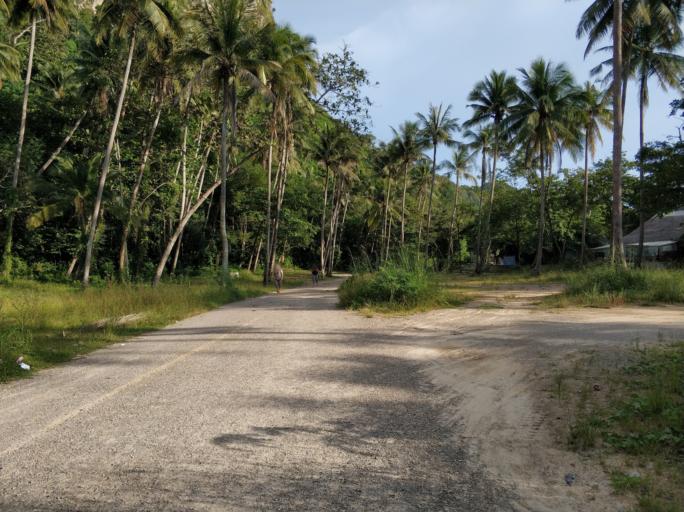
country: TH
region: Phangnga
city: Ban Ao Nang
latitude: 8.0283
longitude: 98.8262
